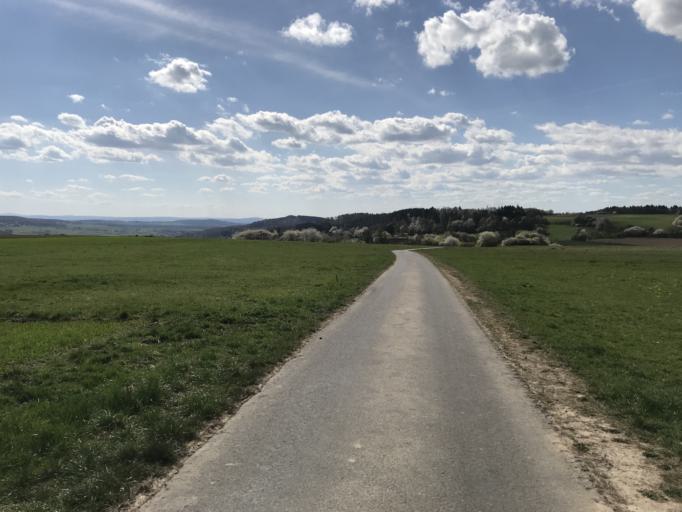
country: DE
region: Hesse
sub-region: Regierungsbezirk Giessen
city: Ebsdorfergrund
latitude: 50.6999
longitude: 8.8362
